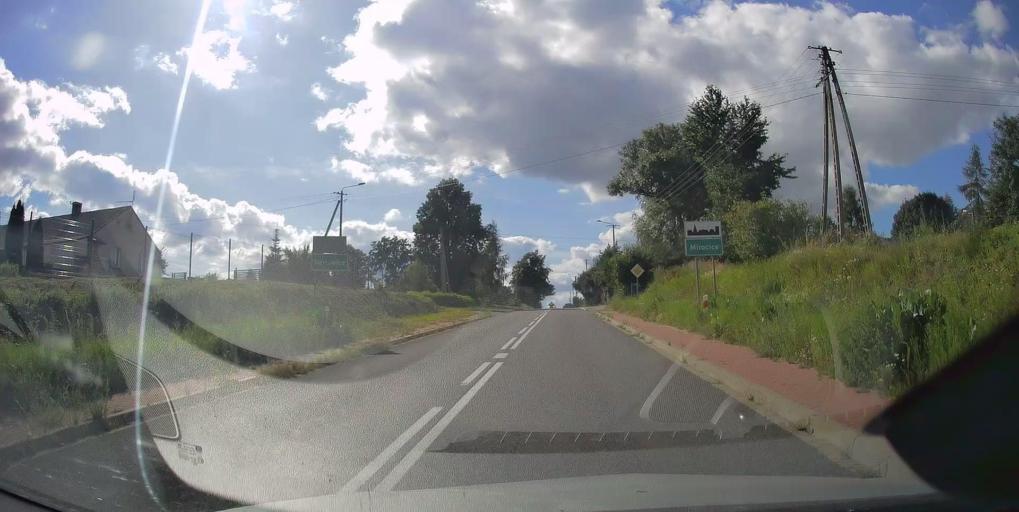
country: PL
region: Swietokrzyskie
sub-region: Powiat kielecki
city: Nowa Slupia
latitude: 50.8827
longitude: 21.0529
